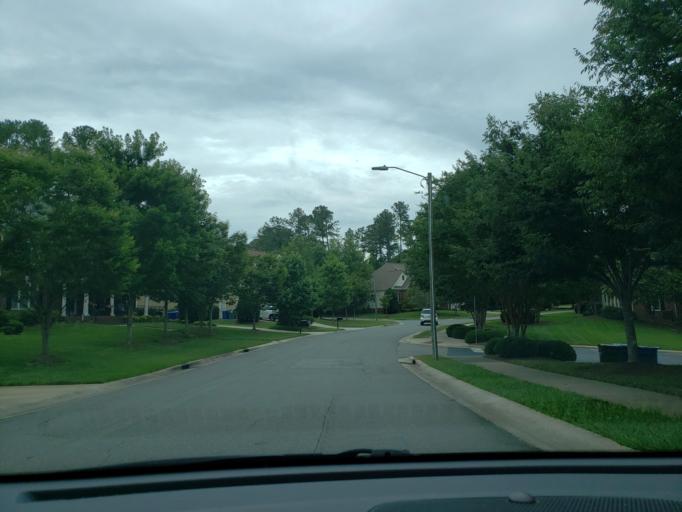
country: US
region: North Carolina
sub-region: Orange County
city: Chapel Hill
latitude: 35.8940
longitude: -78.9783
